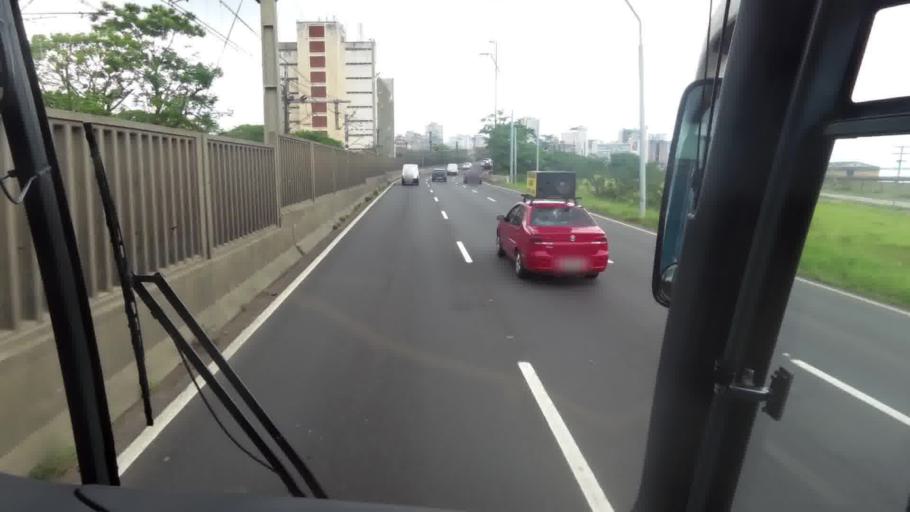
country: BR
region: Rio Grande do Sul
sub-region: Porto Alegre
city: Porto Alegre
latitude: -30.0191
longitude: -51.2161
